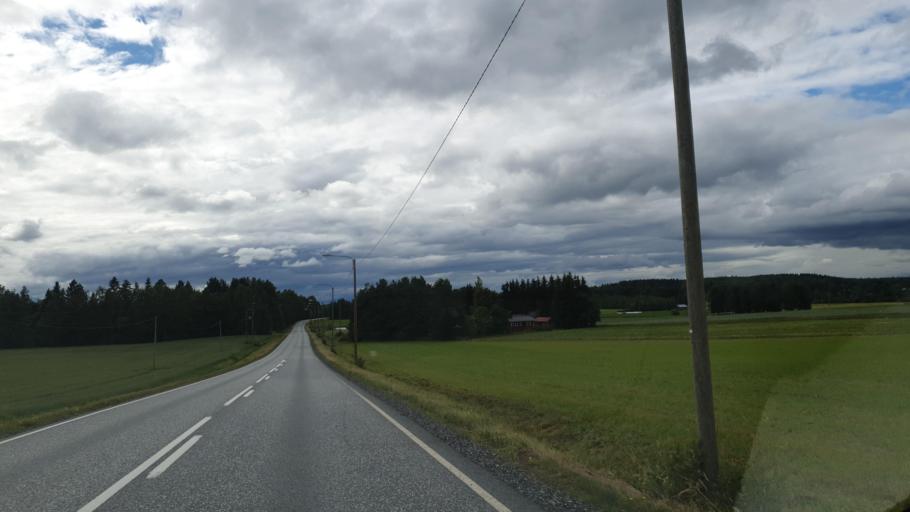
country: FI
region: Northern Savo
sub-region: Ylae-Savo
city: Iisalmi
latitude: 63.5210
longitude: 27.1642
